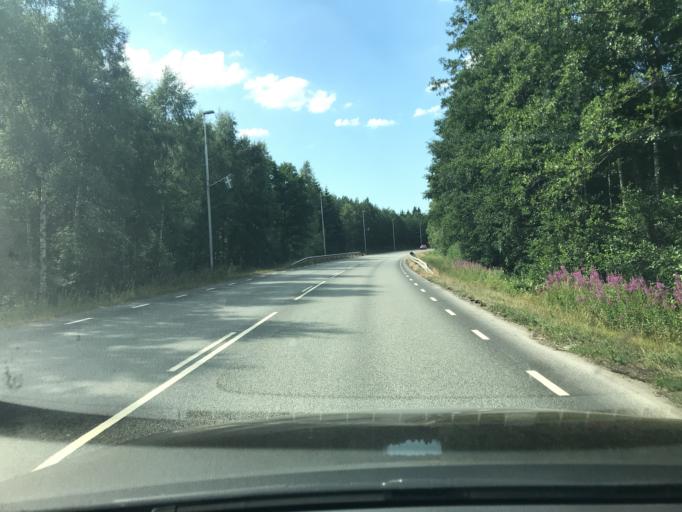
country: SE
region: Skane
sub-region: Hassleholms Kommun
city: Hastveda
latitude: 56.2773
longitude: 13.9369
